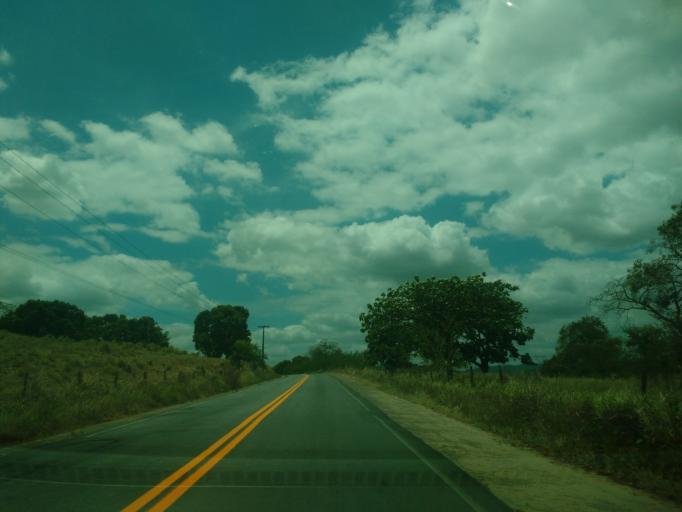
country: BR
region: Alagoas
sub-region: Uniao Dos Palmares
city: Uniao dos Palmares
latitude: -9.1416
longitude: -36.0413
